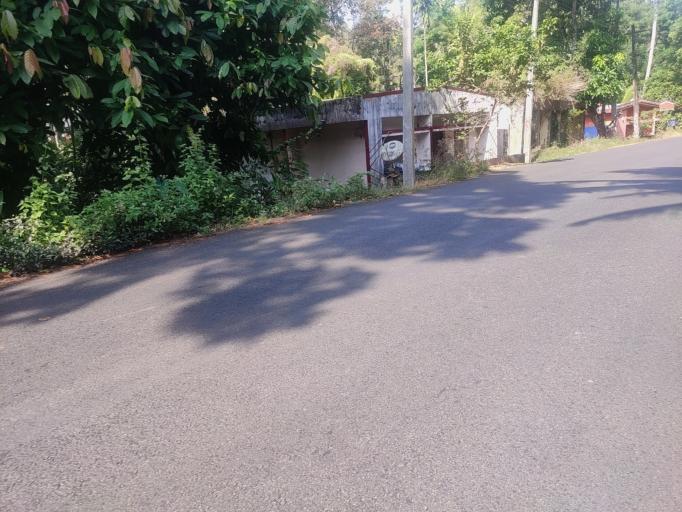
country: IN
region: Kerala
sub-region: Pattanamtitta
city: Pathanamthitta
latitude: 9.4392
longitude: 76.8796
